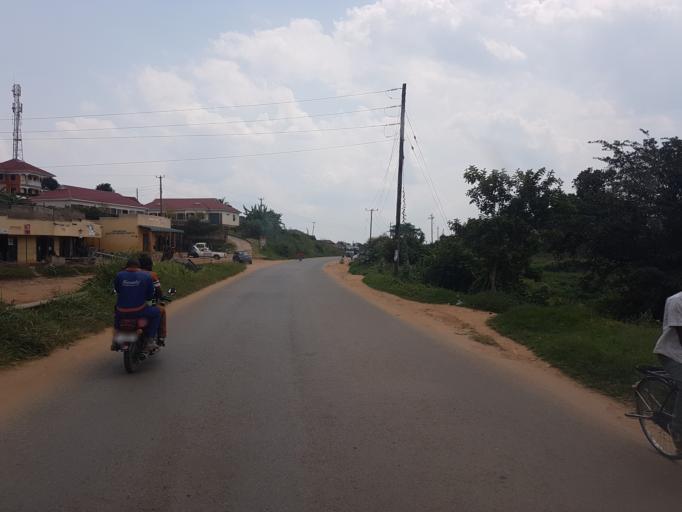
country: UG
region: Western Region
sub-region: Bushenyi District
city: Bushenyi
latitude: -0.5447
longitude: 30.1356
